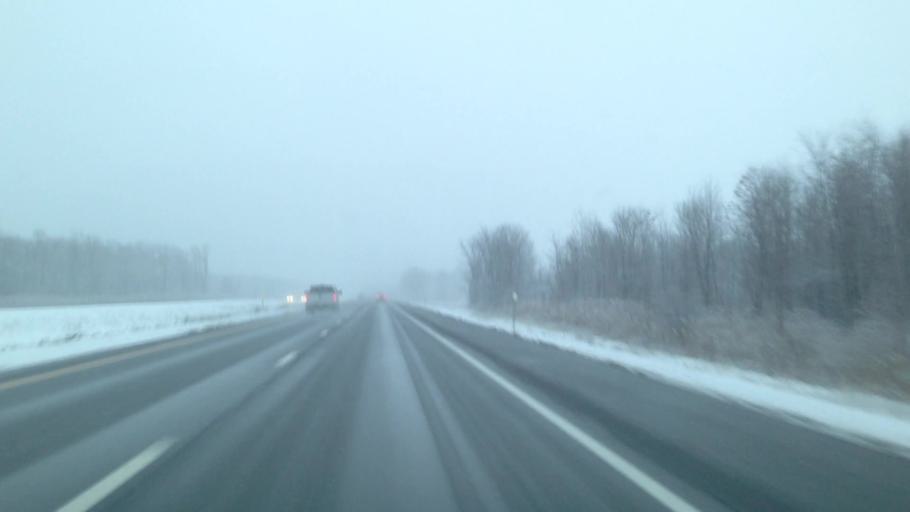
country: US
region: New York
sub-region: Madison County
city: Chittenango
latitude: 43.0938
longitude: -75.8259
